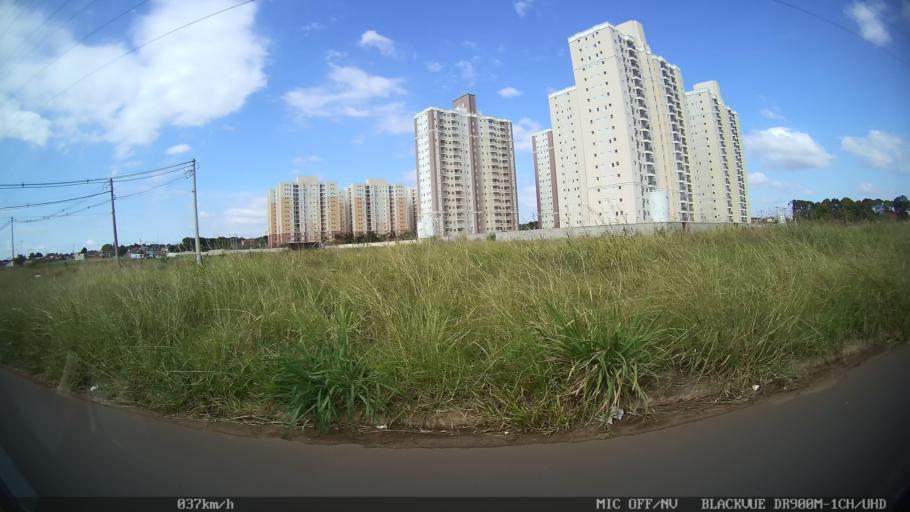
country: BR
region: Sao Paulo
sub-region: Americana
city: Americana
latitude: -22.7214
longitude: -47.3191
